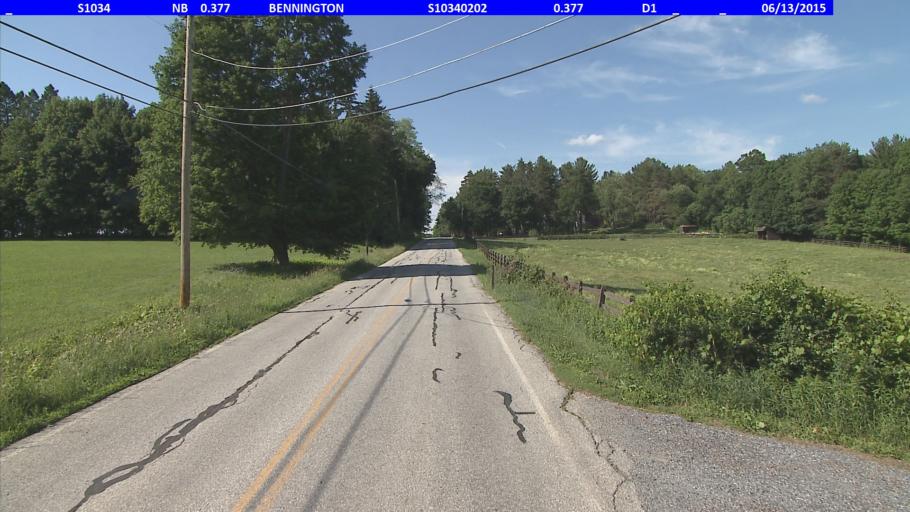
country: US
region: Vermont
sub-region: Bennington County
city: Bennington
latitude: 42.8575
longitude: -73.2061
